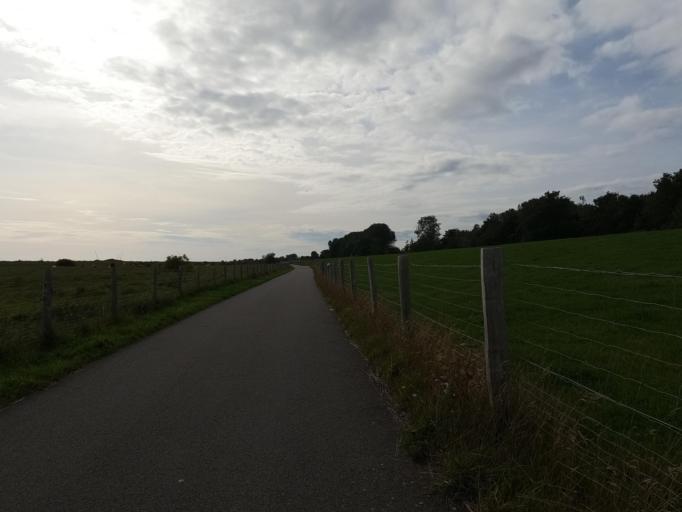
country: DE
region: Schleswig-Holstein
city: Dahme
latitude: 54.2519
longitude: 11.0800
